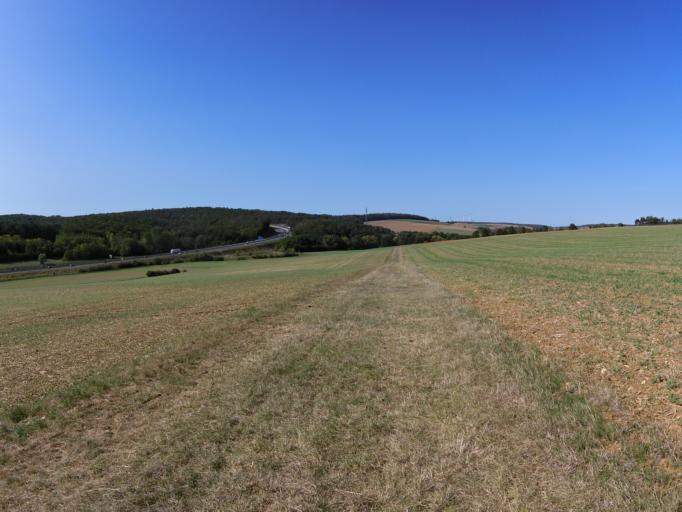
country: DE
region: Bavaria
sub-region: Regierungsbezirk Unterfranken
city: Waldbrunn
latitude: 49.7642
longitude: 9.7848
